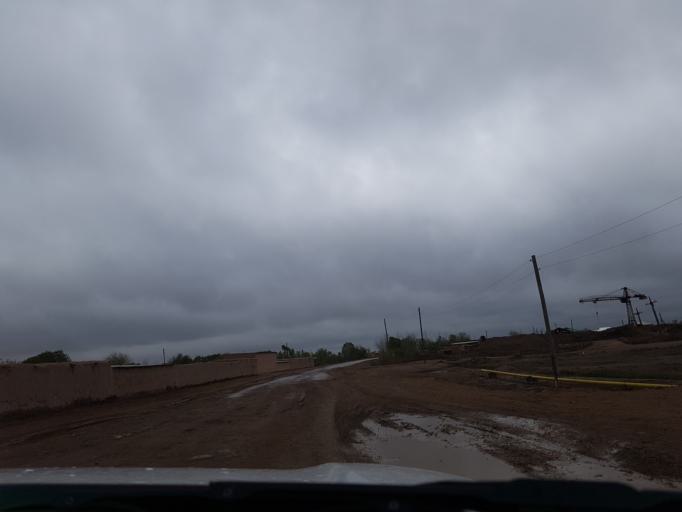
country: TM
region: Lebap
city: Sayat
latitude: 38.4550
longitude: 64.3576
